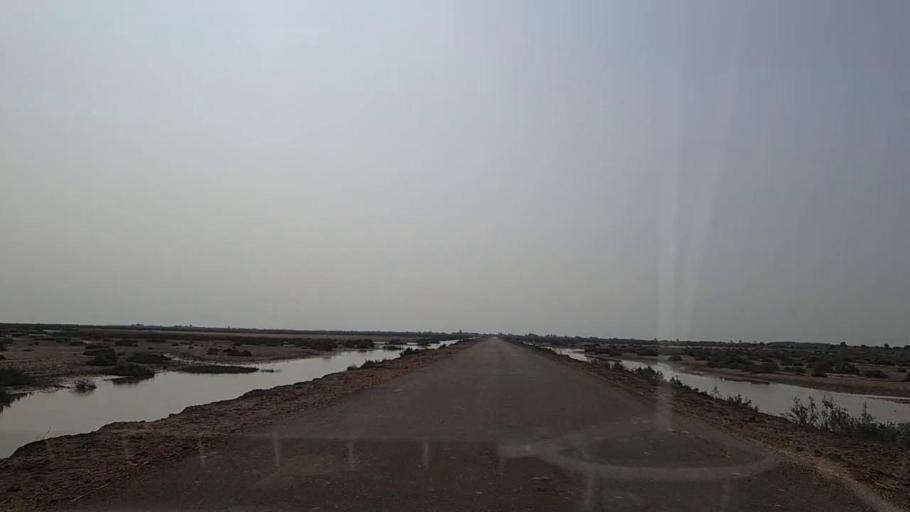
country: PK
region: Sindh
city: Chuhar Jamali
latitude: 24.2095
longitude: 67.8591
